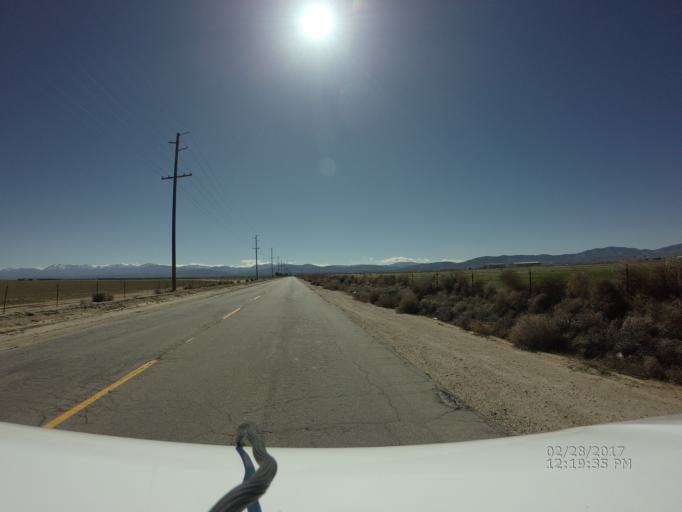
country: US
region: California
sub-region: Los Angeles County
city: Palmdale
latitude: 34.6276
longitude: -118.0587
